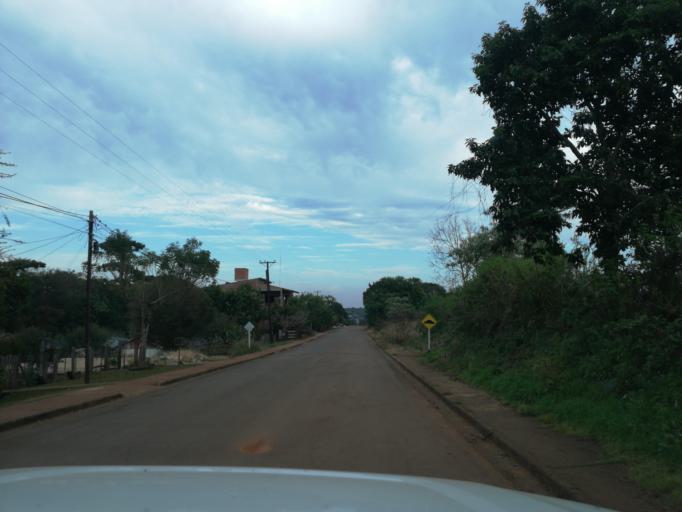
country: AR
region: Misiones
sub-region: Departamento de San Pedro
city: San Pedro
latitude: -26.6257
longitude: -54.1010
